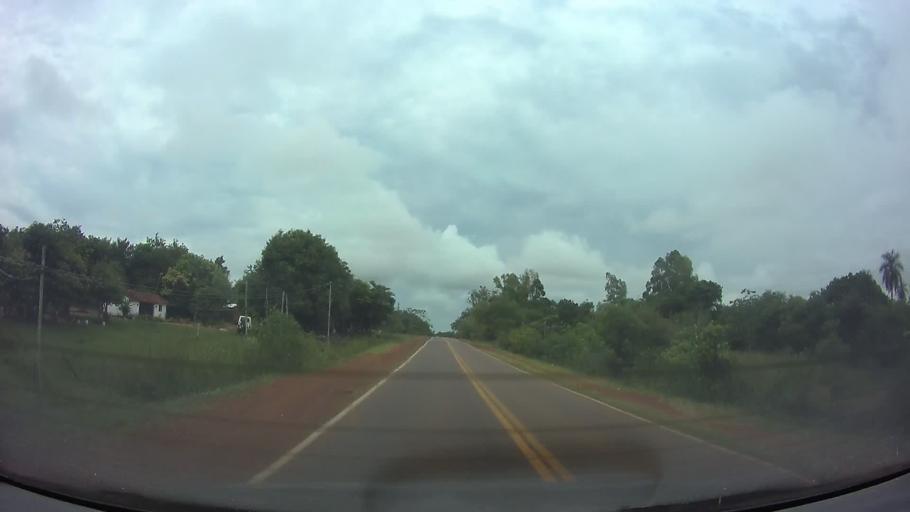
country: PY
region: Paraguari
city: Carapegua
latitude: -25.7971
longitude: -57.1994
